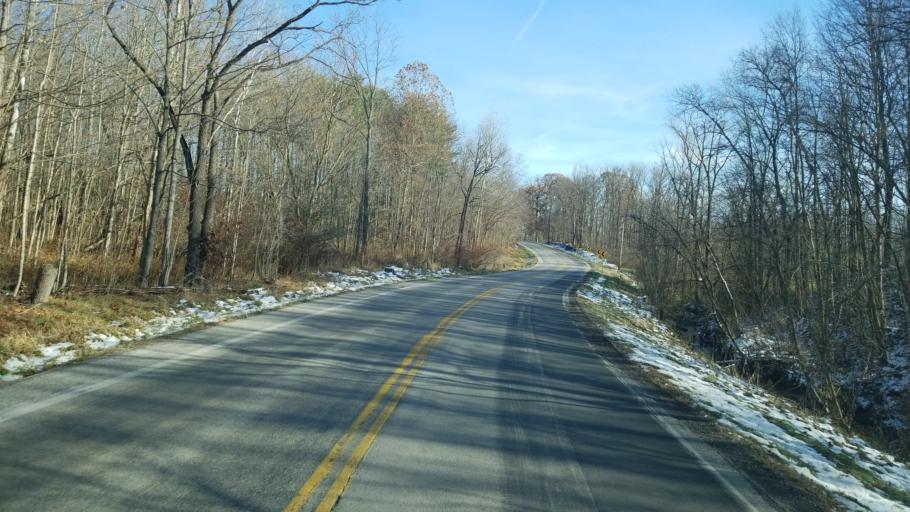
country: US
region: Ohio
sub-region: Huron County
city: Wakeman
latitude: 41.2389
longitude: -82.3712
